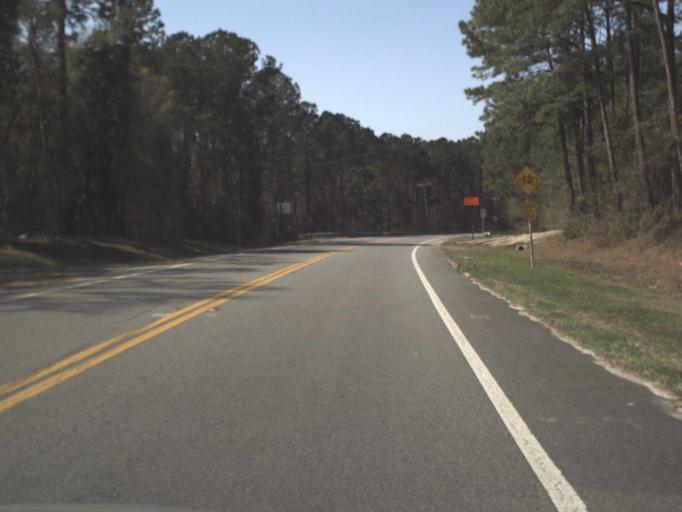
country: US
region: Florida
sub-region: Gadsden County
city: Havana
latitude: 30.5875
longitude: -84.4881
